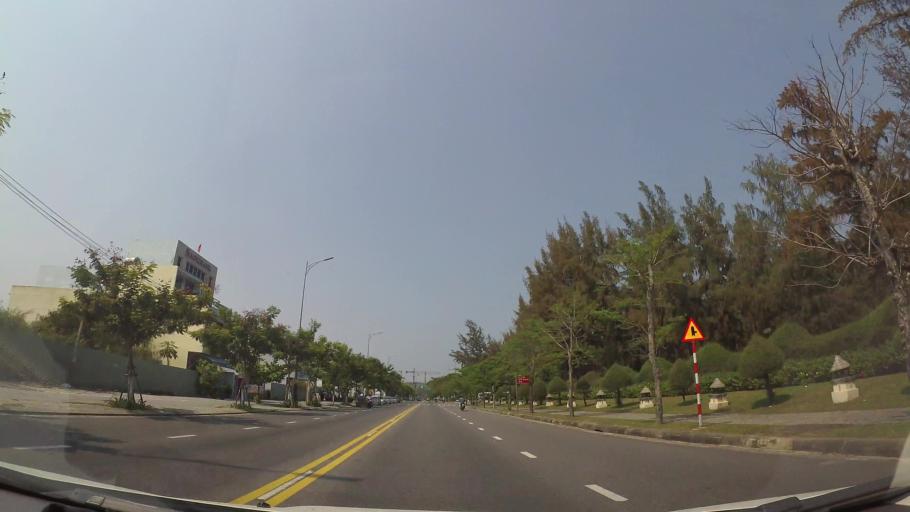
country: VN
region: Da Nang
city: Ngu Hanh Son
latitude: 15.9976
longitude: 108.2676
